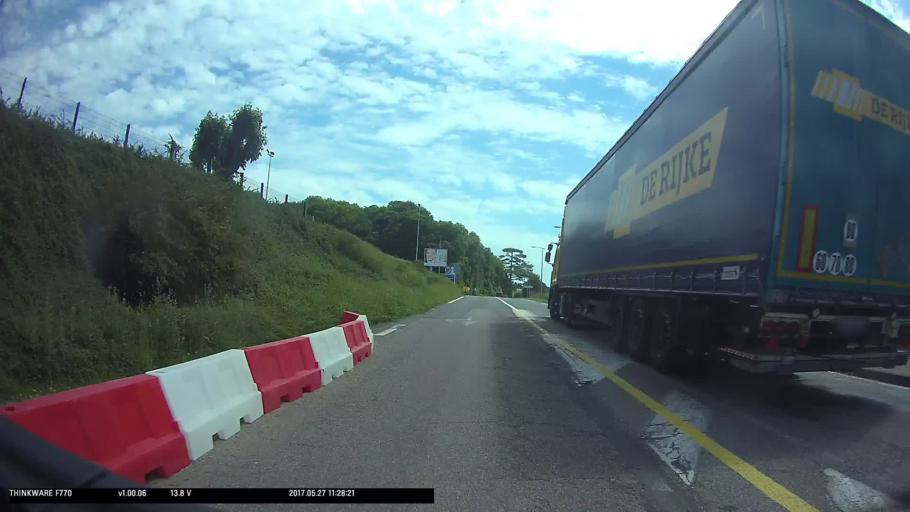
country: FR
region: Picardie
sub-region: Departement de l'Oise
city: Trie-Chateau
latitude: 49.2886
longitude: 1.8096
